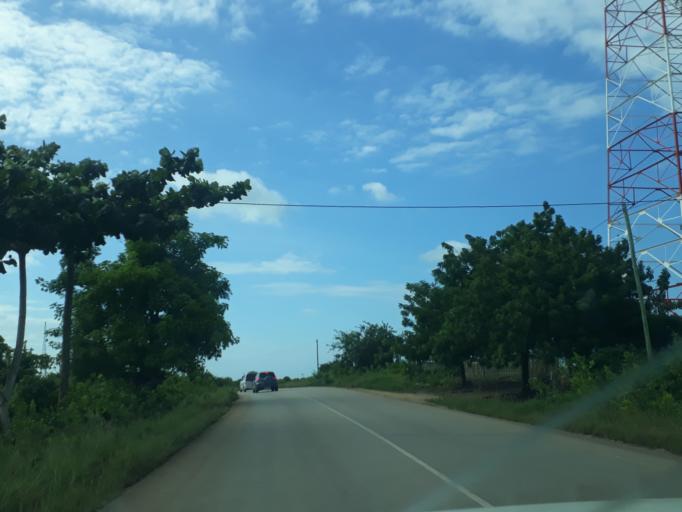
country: TZ
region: Zanzibar North
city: Nungwi
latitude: -5.7618
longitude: 39.3018
